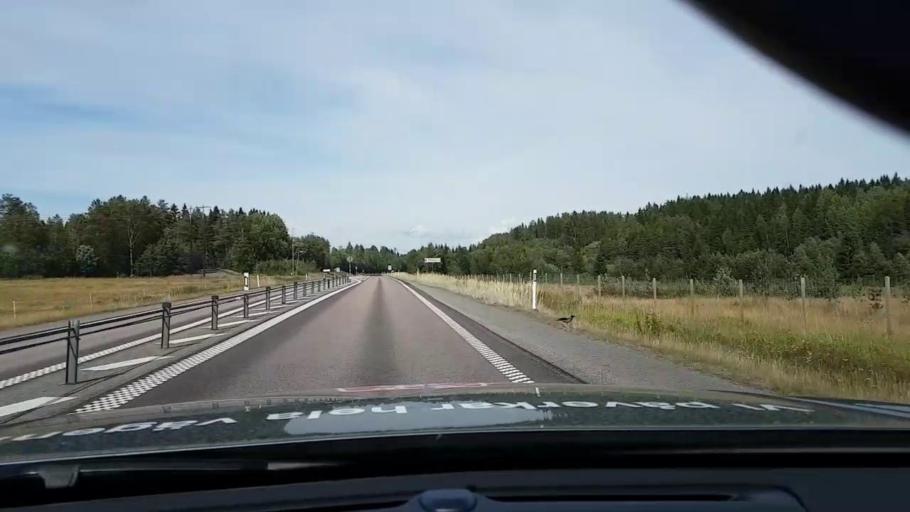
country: SE
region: Vaesternorrland
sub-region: OErnskoeldsviks Kommun
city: Husum
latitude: 63.4176
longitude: 19.2054
